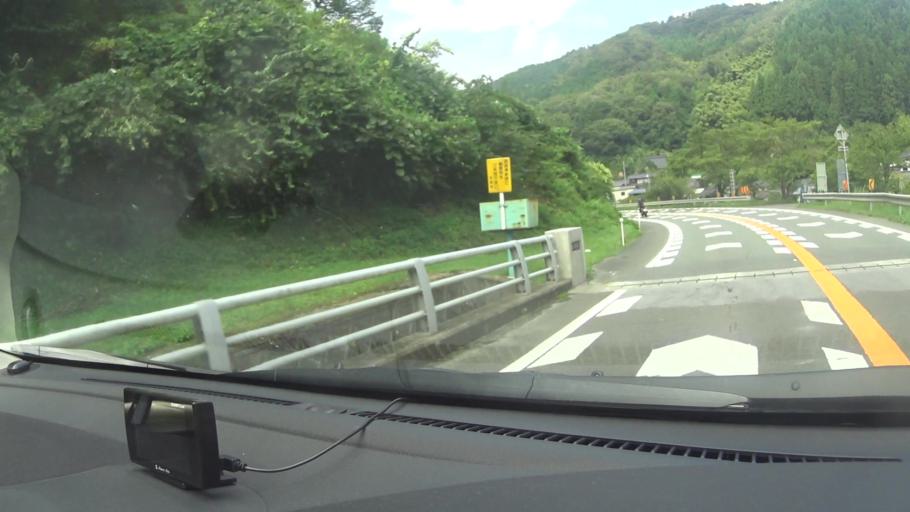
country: JP
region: Kyoto
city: Ayabe
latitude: 35.2446
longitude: 135.2941
